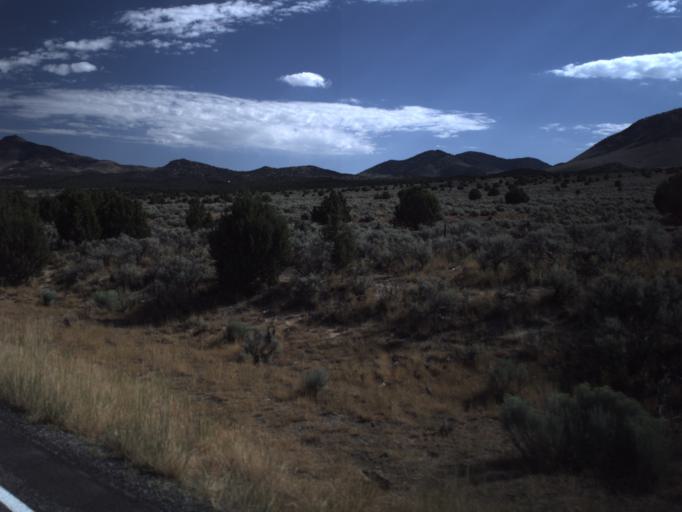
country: US
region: Utah
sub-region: Juab County
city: Mona
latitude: 39.8475
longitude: -112.1381
